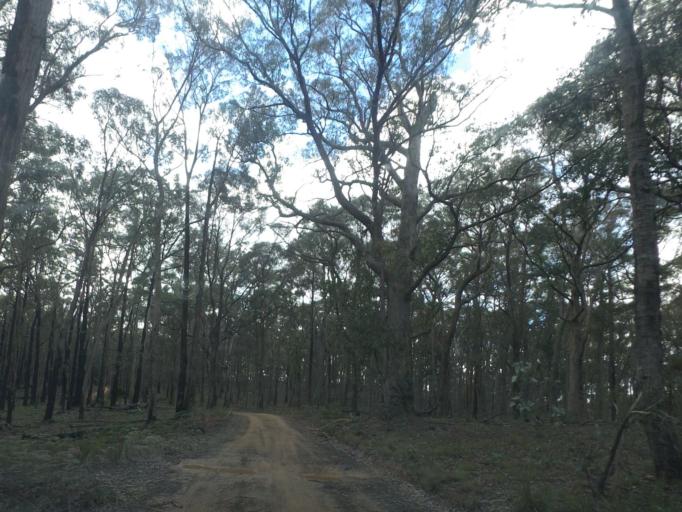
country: AU
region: Victoria
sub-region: Moorabool
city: Bacchus Marsh
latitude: -37.4569
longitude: 144.3230
